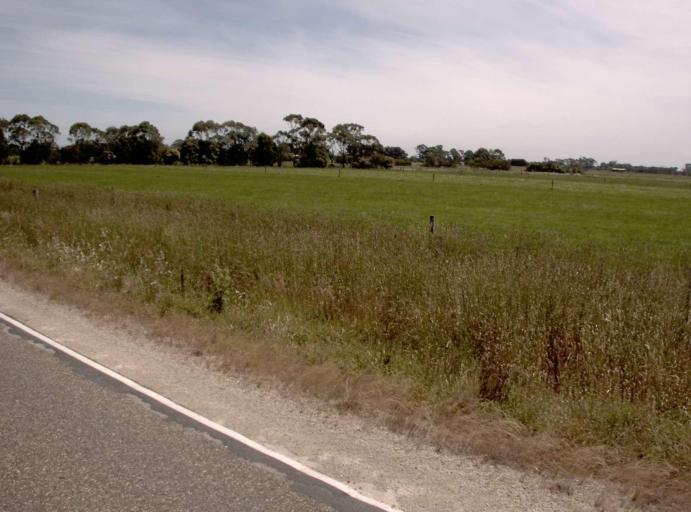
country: AU
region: Victoria
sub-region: Wellington
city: Heyfield
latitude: -38.0470
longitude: 146.8758
